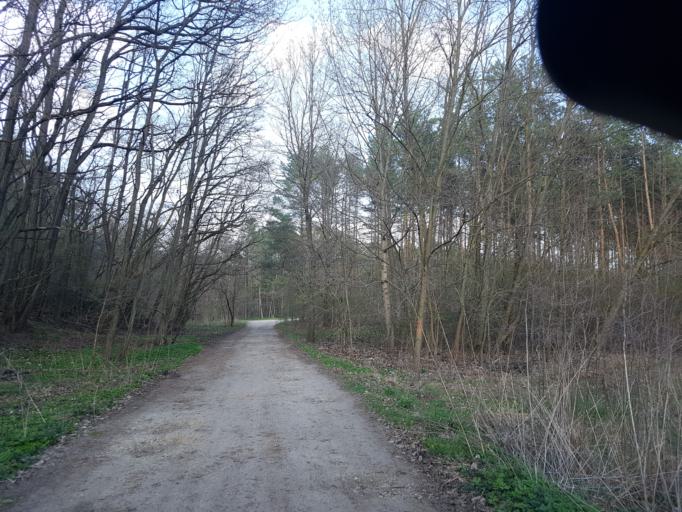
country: DE
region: Brandenburg
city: Trobitz
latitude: 51.6021
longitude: 13.4594
